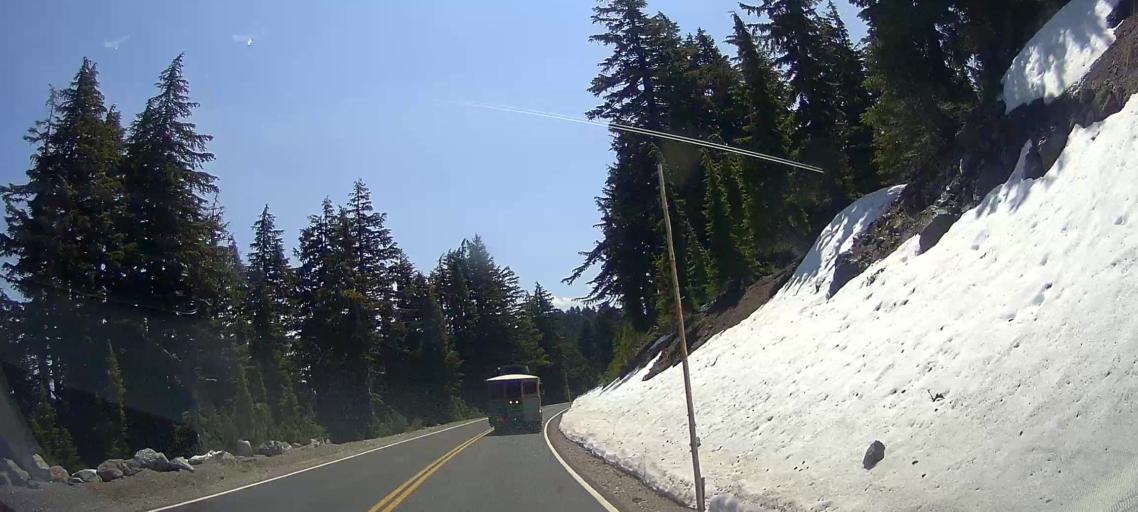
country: US
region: Oregon
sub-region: Jackson County
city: Shady Cove
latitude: 42.9821
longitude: -122.1315
